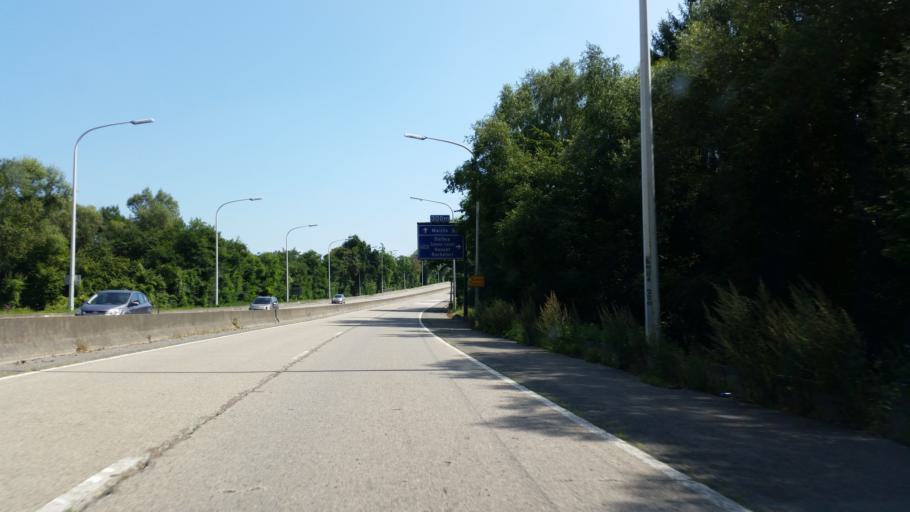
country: BE
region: Wallonia
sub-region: Province de Namur
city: Hamois
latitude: 50.2786
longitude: 5.2273
